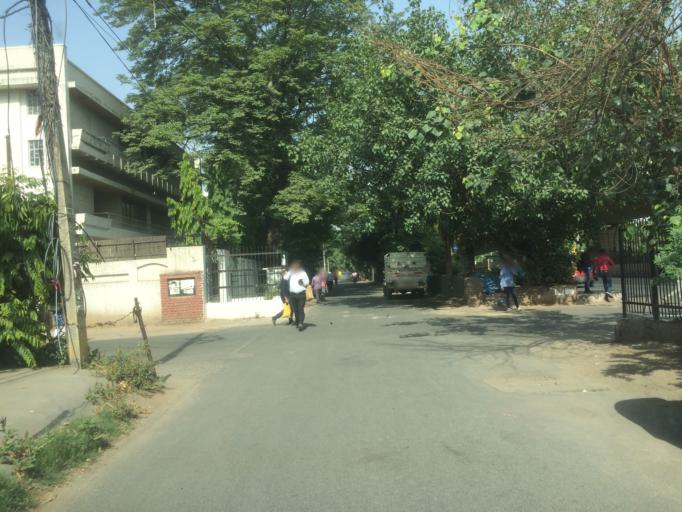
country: IN
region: NCT
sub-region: New Delhi
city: New Delhi
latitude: 28.5651
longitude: 77.2475
